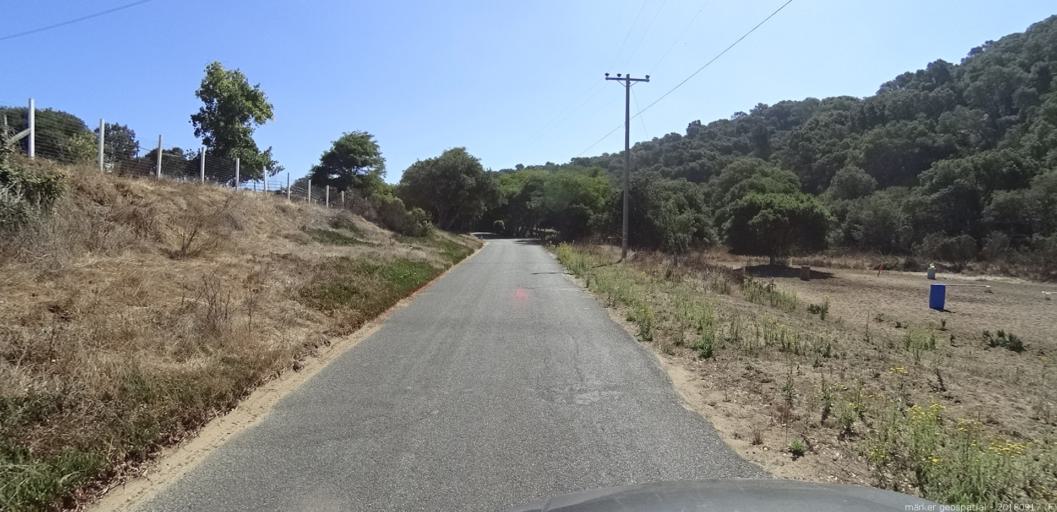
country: US
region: California
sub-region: Monterey County
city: Elkhorn
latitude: 36.8253
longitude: -121.7067
